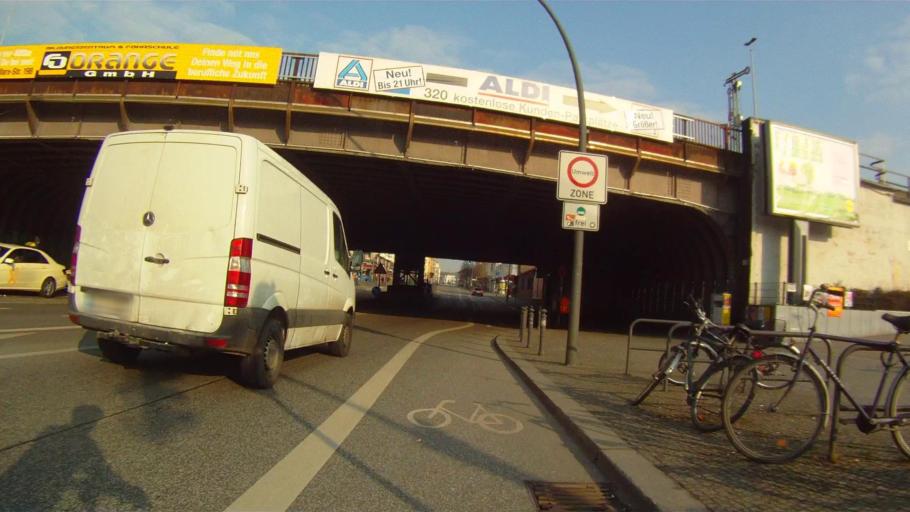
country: DE
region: Berlin
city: Berlin Treptow
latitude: 52.4688
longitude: 13.4419
